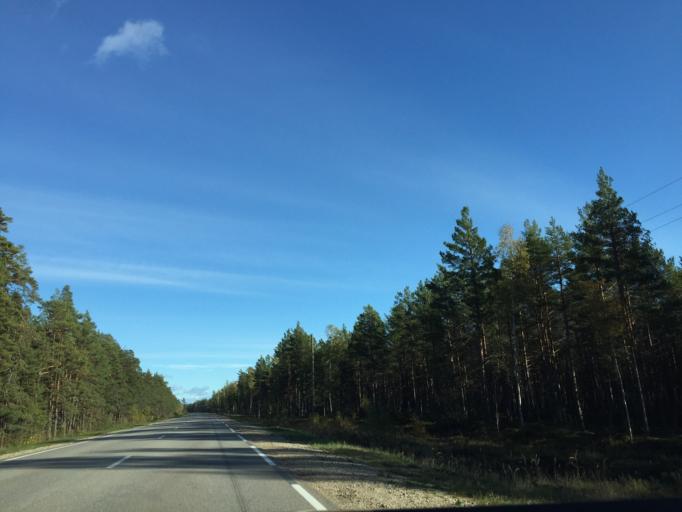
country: LV
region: Engure
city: Smarde
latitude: 57.0353
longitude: 23.4232
